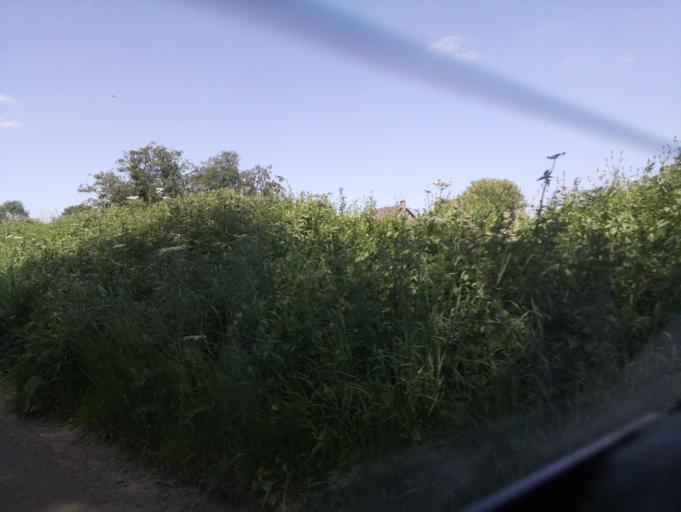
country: GB
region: England
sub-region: Wiltshire
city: Bremhill
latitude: 51.5052
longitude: -2.0517
